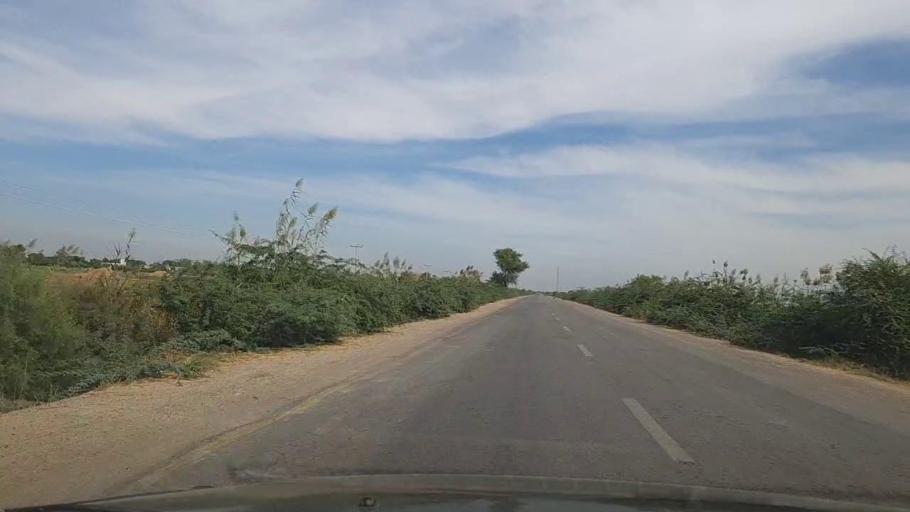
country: PK
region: Sindh
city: Thatta
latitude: 24.8032
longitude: 67.9680
